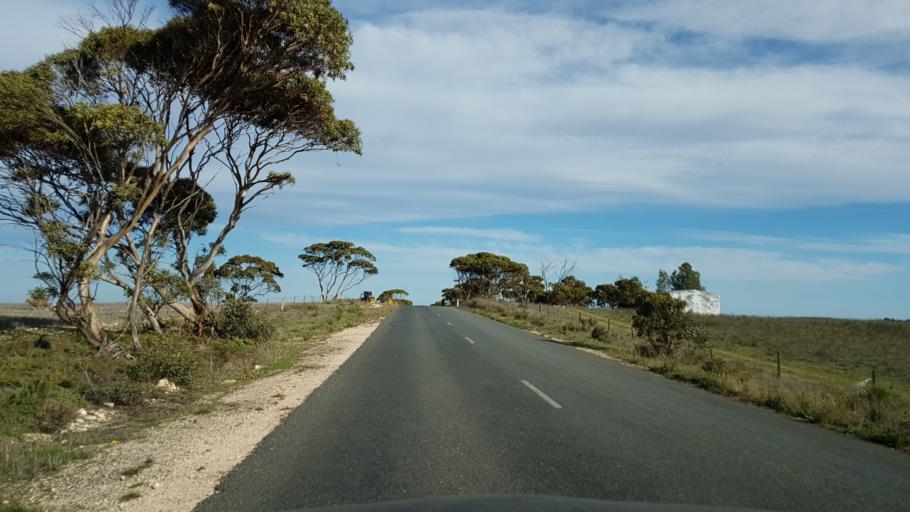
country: AU
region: South Australia
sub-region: Murray Bridge
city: Tailem Bend
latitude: -35.1832
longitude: 139.4567
